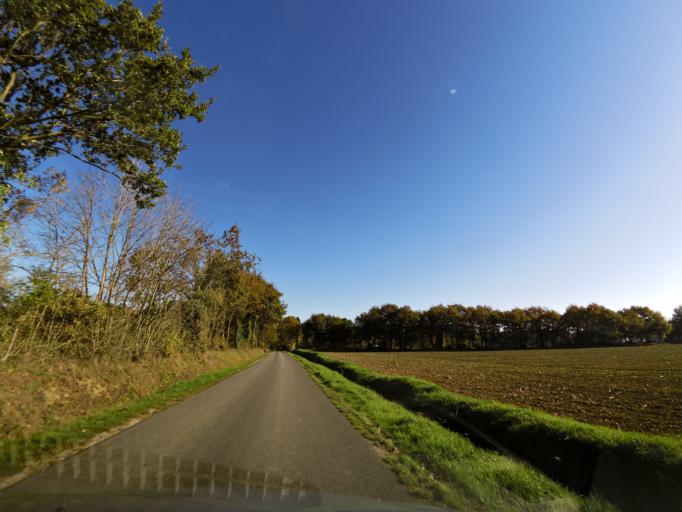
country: FR
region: Brittany
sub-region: Departement d'Ille-et-Vilaine
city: Bain-de-Bretagne
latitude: 47.8712
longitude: -1.7050
